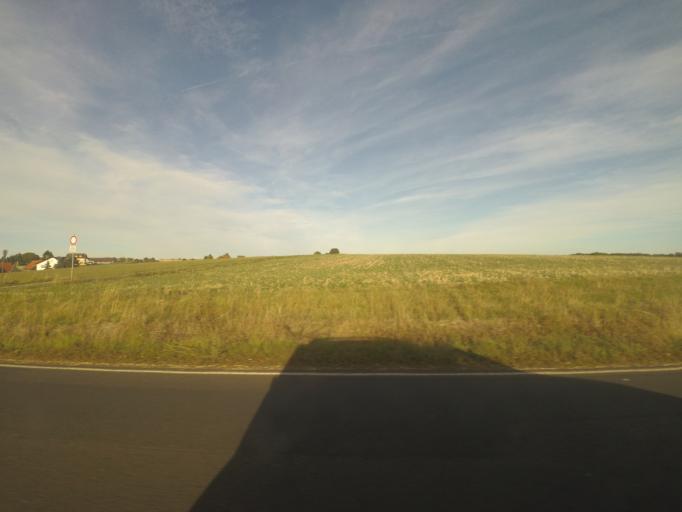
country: DE
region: Hesse
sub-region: Regierungsbezirk Darmstadt
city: Steinau an der Strasse
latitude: 50.3486
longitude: 9.3972
